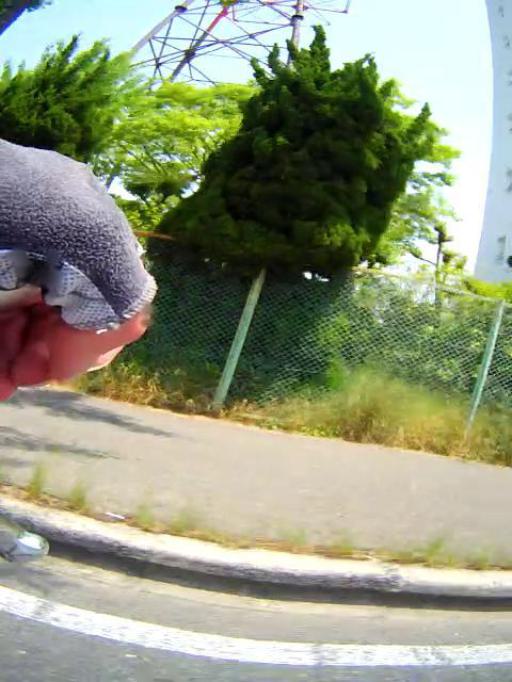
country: JP
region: Osaka
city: Suita
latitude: 34.7725
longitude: 135.4955
